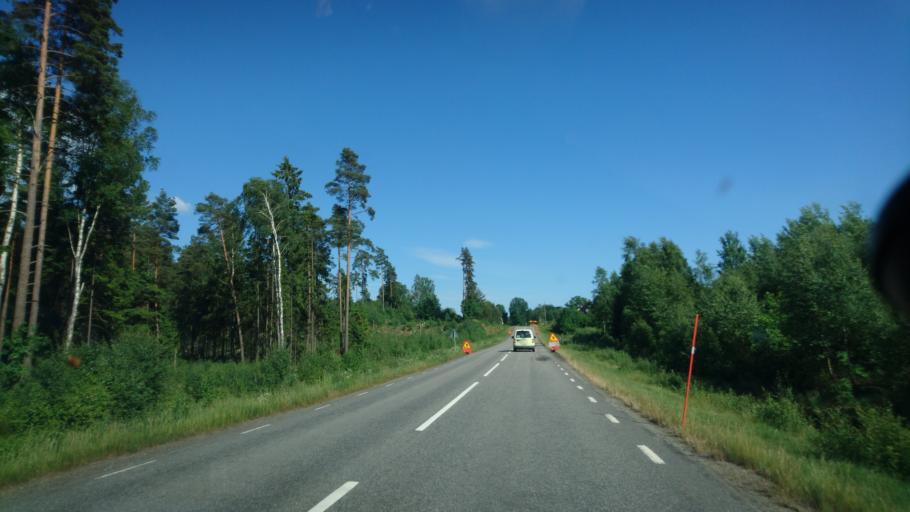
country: SE
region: Skane
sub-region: Osby Kommun
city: Lonsboda
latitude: 56.4088
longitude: 14.3119
